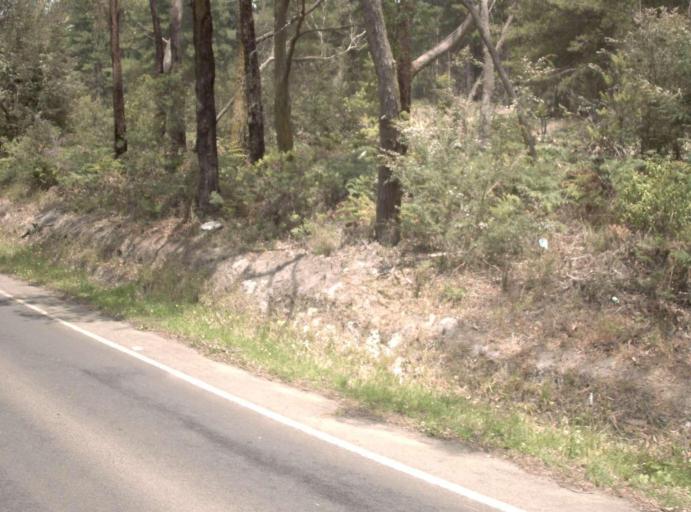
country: AU
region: Victoria
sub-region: Latrobe
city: Traralgon
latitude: -38.2734
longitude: 146.6923
